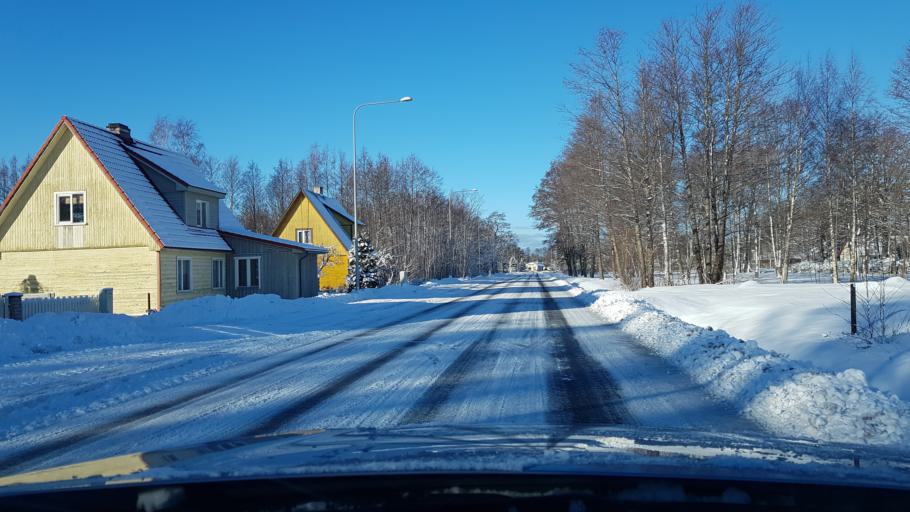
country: EE
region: Hiiumaa
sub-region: Kaerdla linn
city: Kardla
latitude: 58.9876
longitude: 22.7526
